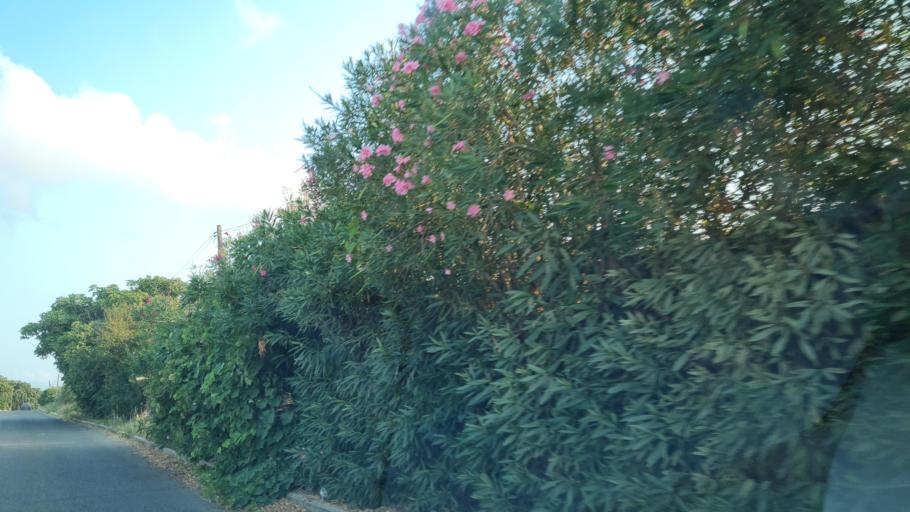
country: IT
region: Latium
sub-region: Provincia di Viterbo
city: Montalto di Castro
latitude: 42.3440
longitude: 11.6100
